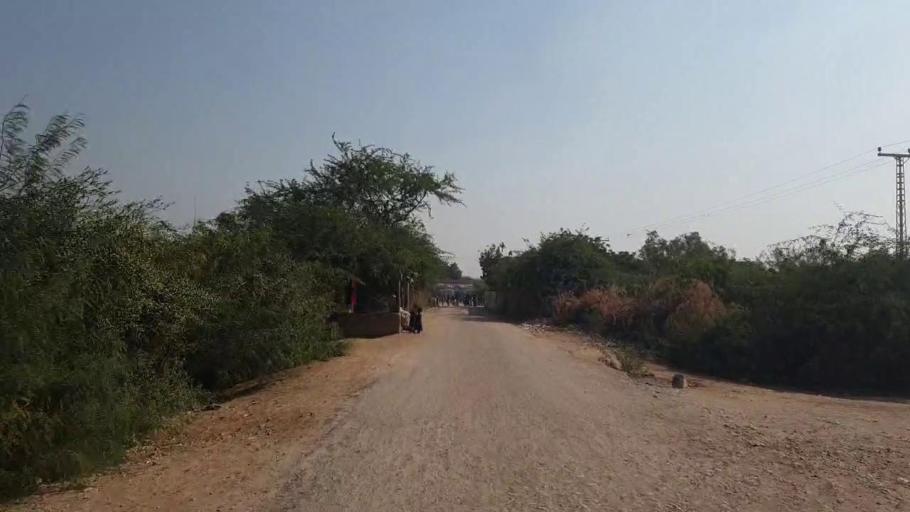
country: PK
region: Sindh
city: Kotri
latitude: 25.3218
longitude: 68.2371
